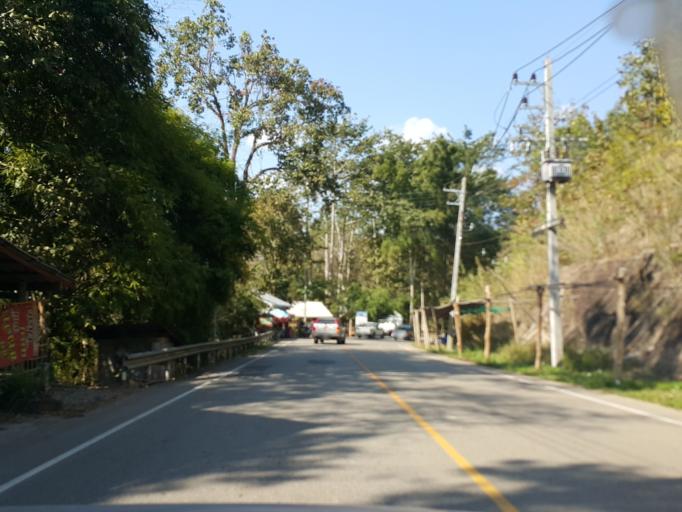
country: TH
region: Chiang Mai
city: Mae Wang
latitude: 18.6393
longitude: 98.6997
